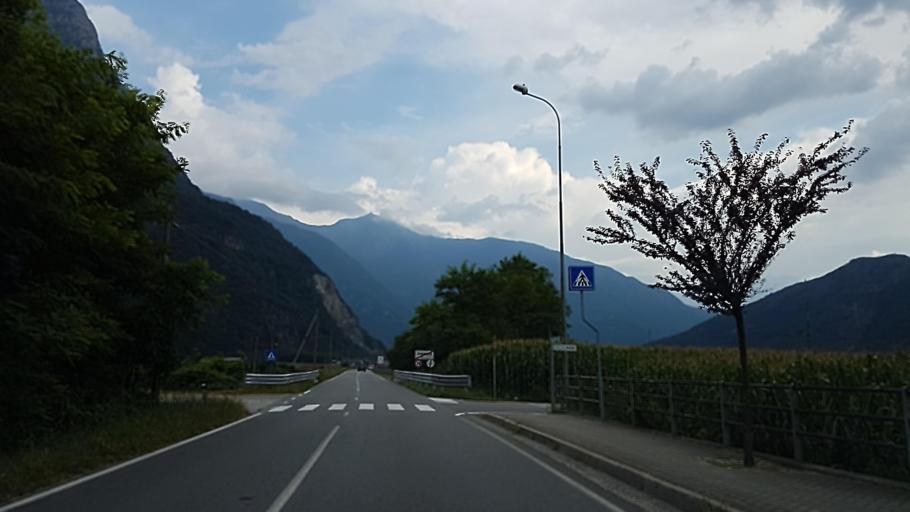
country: IT
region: Lombardy
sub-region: Provincia di Sondrio
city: Era
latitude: 46.2448
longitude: 9.4256
